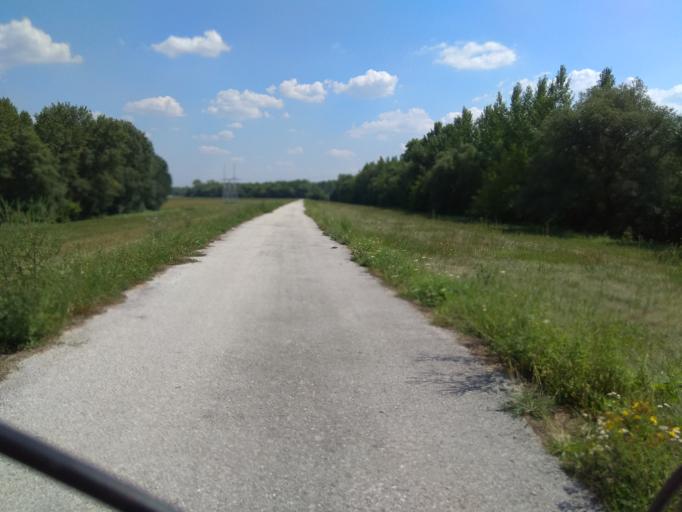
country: SK
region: Trnavsky
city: Gabcikovo
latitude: 47.8037
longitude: 17.6467
